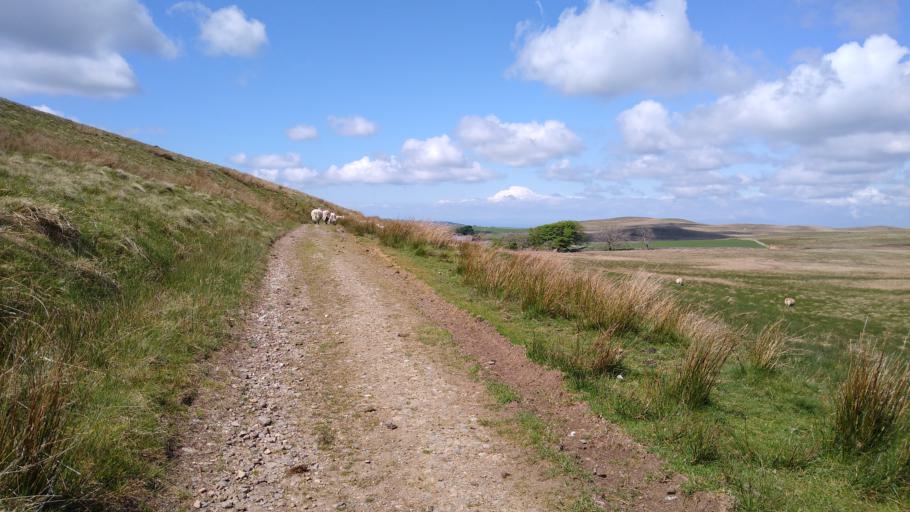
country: GB
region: England
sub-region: Cumbria
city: Wigton
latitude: 54.7179
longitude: -3.1256
